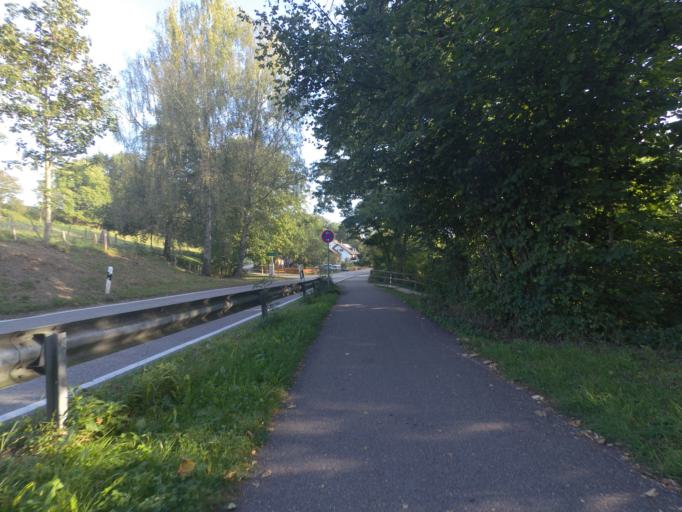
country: DE
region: Bavaria
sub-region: Upper Bavaria
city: Laufen
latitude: 47.9115
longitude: 12.9145
